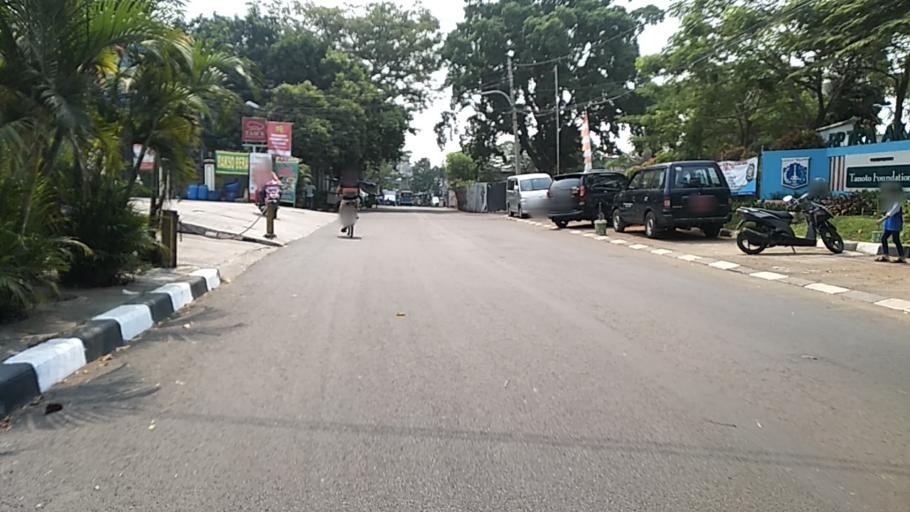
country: ID
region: Jakarta Raya
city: Jakarta
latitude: -6.2331
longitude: 106.8507
